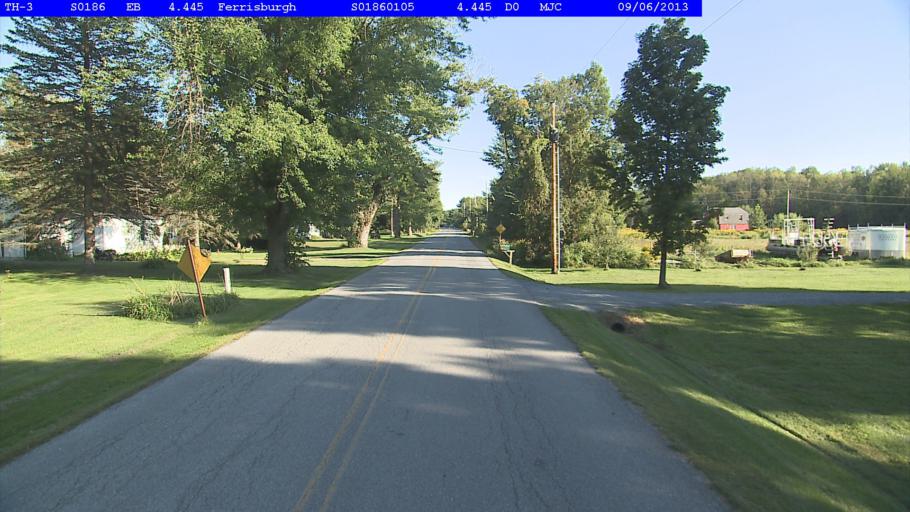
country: US
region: Vermont
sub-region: Addison County
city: Vergennes
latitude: 44.1655
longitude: -73.2961
